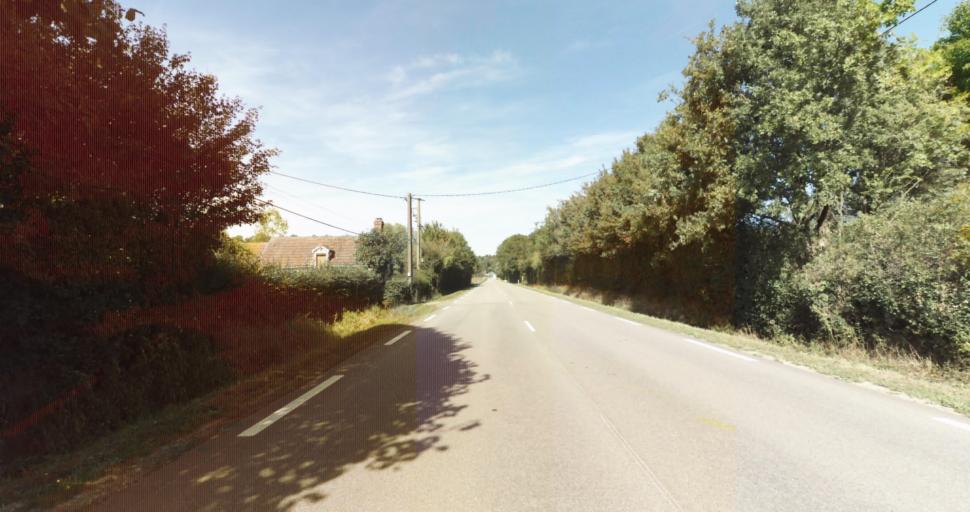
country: FR
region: Lower Normandy
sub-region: Departement de l'Orne
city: Gace
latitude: 48.7227
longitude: 0.2321
